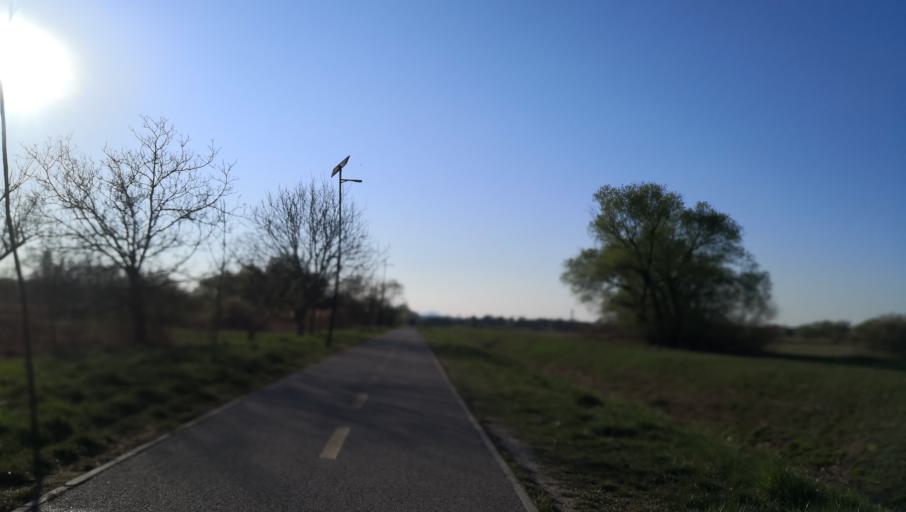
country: HU
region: Pest
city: Csomor
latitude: 47.5128
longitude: 19.2321
